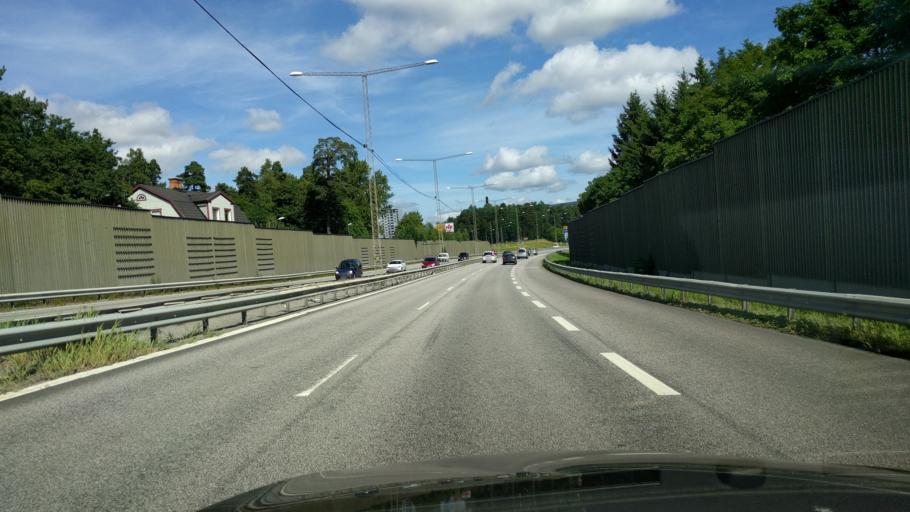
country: SE
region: Stockholm
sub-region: Taby Kommun
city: Taby
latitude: 59.4308
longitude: 18.0657
